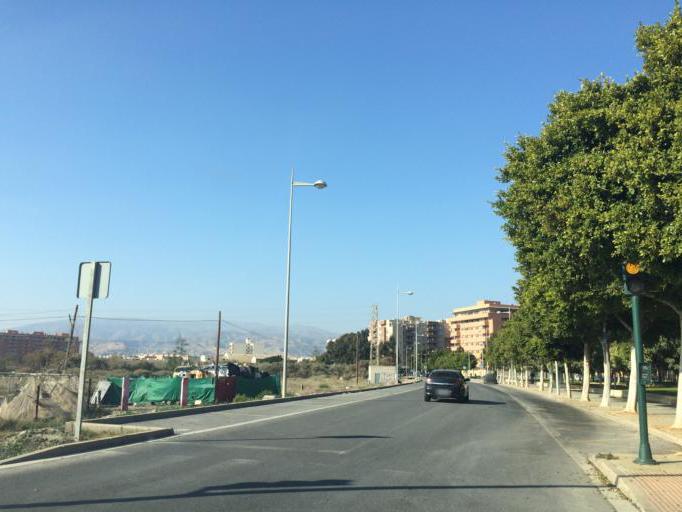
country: ES
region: Andalusia
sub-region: Provincia de Almeria
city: Almeria
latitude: 36.8343
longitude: -2.4325
